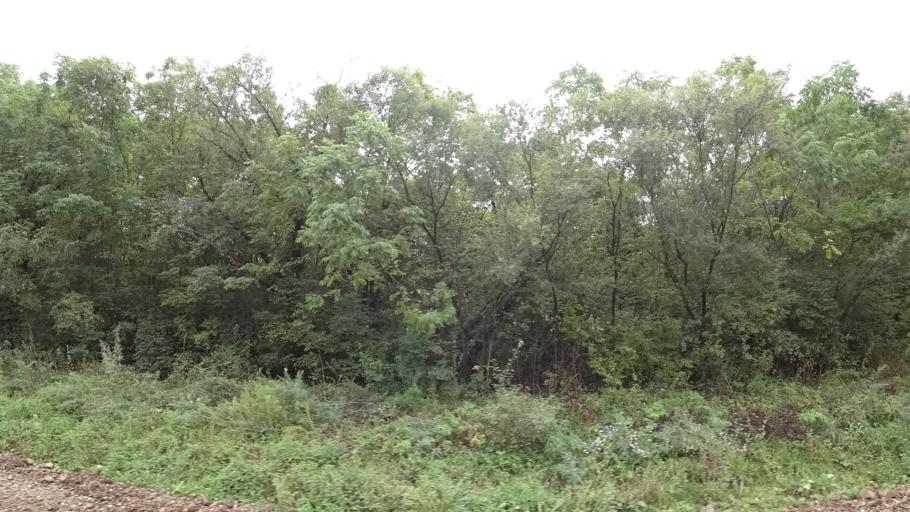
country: RU
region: Primorskiy
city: Lyalichi
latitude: 44.0790
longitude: 132.4511
